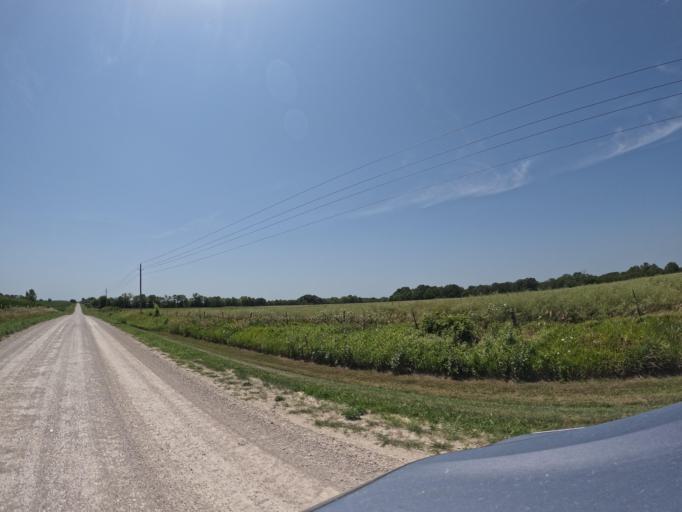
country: US
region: Iowa
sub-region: Henry County
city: Mount Pleasant
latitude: 40.9222
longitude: -91.6458
